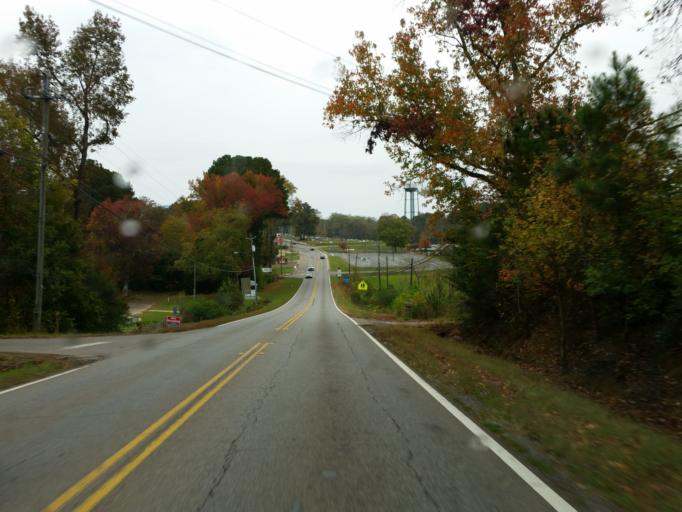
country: US
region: Georgia
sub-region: Pickens County
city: Jasper
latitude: 34.4659
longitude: -84.4388
